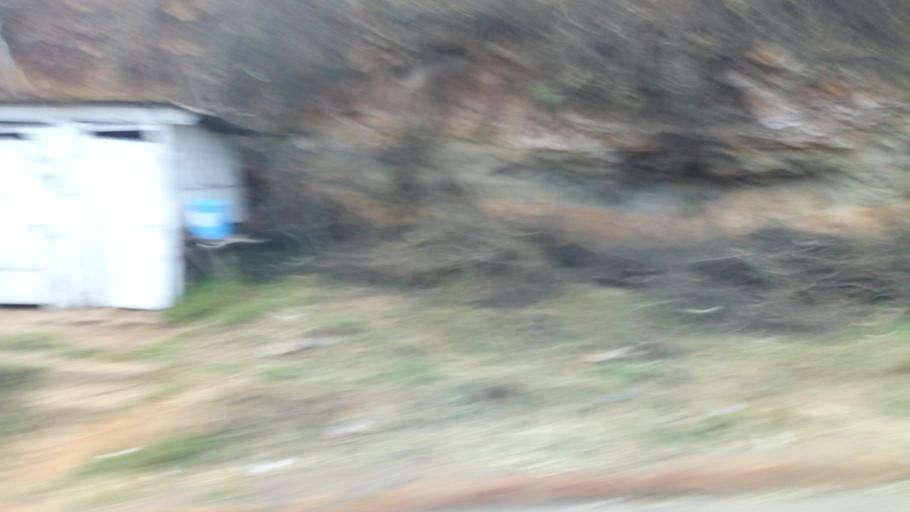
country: KE
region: Kiambu
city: Limuru
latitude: -1.0670
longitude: 36.6015
